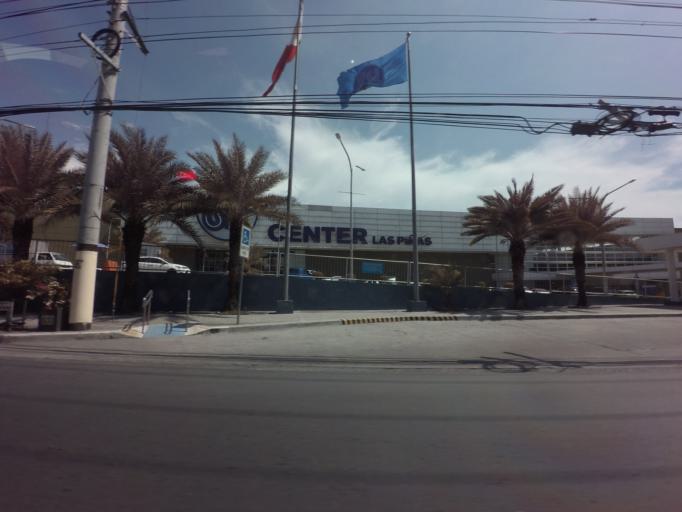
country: PH
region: Calabarzon
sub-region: Province of Rizal
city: Las Pinas
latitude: 14.4496
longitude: 120.9811
